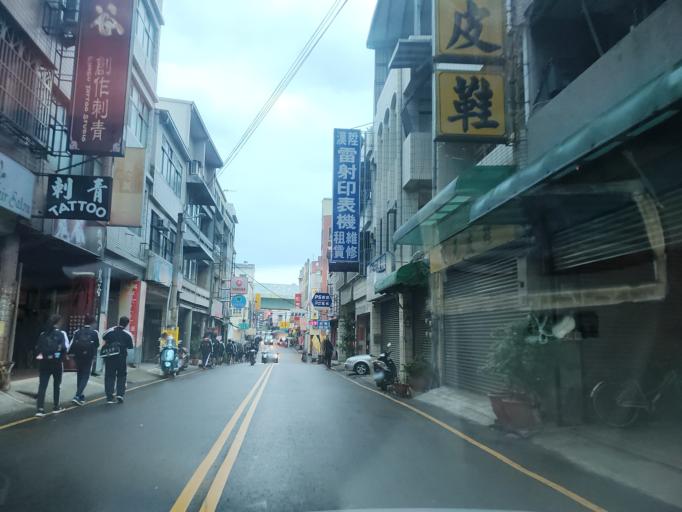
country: TW
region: Taiwan
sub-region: Miaoli
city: Miaoli
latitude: 24.5560
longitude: 120.8163
